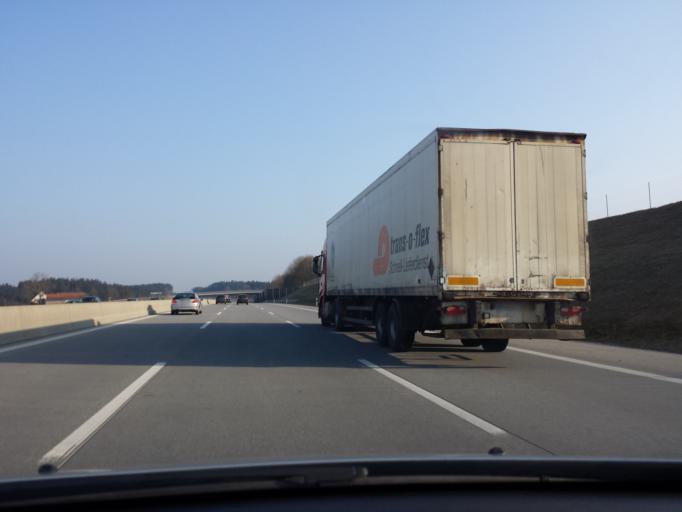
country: DE
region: Bavaria
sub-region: Swabia
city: Eurasburg
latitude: 48.3769
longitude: 11.0918
